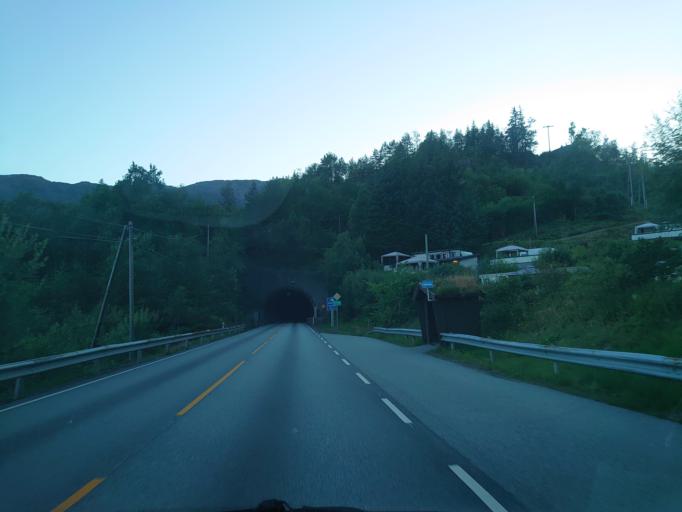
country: NO
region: Hordaland
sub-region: Osteroy
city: Lonevag
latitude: 60.6988
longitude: 5.5799
